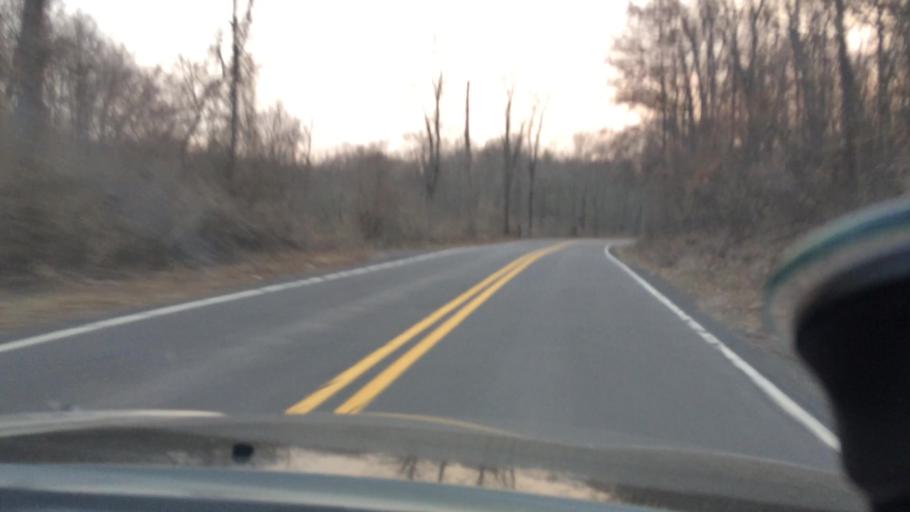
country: US
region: Pennsylvania
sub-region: Luzerne County
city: Freeland
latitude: 41.0777
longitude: -75.9064
